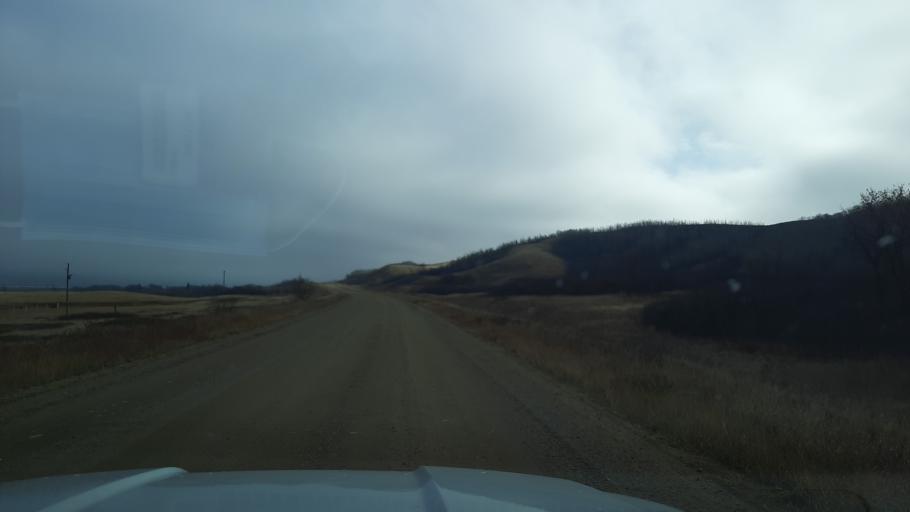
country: CA
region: Saskatchewan
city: White City
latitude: 50.7808
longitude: -104.1561
